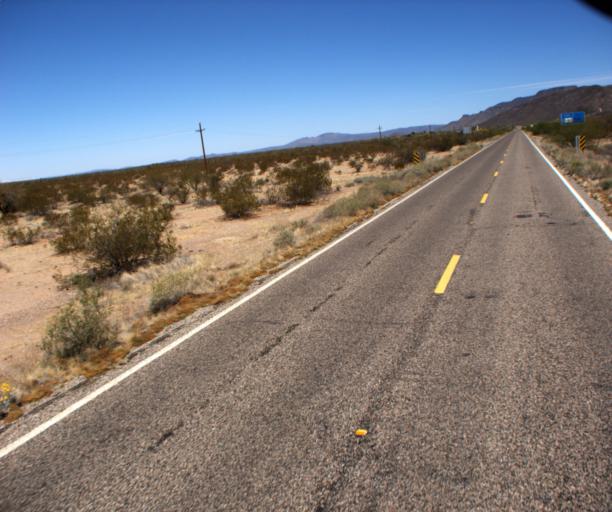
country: US
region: Arizona
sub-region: Pima County
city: Ajo
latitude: 32.2495
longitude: -112.7461
